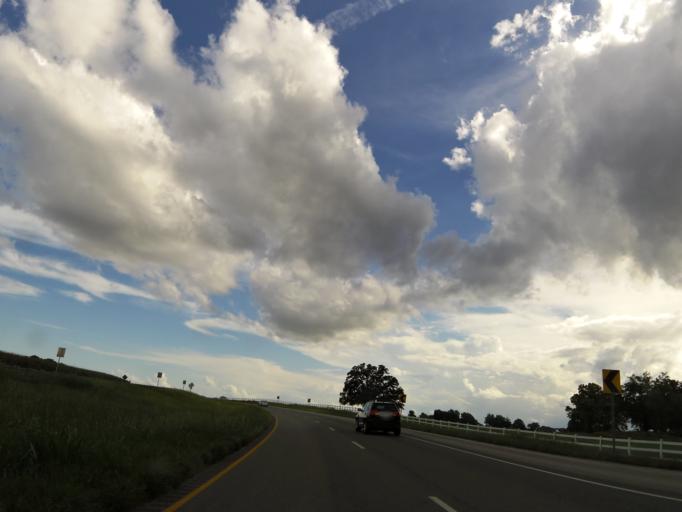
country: US
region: Kentucky
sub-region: Christian County
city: Oak Grove
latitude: 36.7629
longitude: -87.4717
